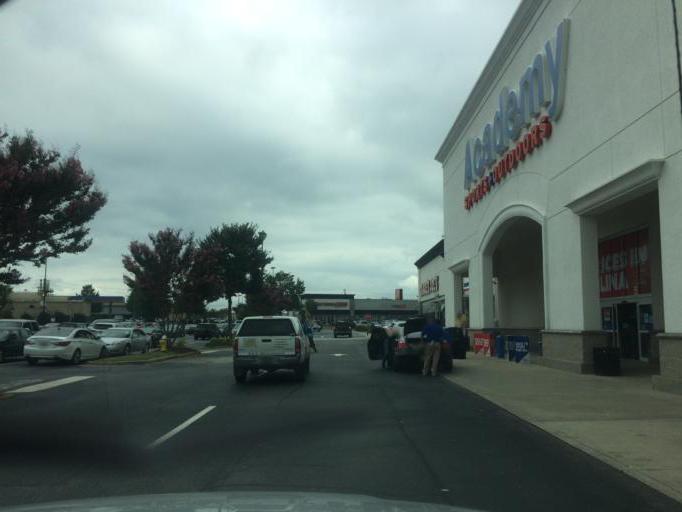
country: US
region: South Carolina
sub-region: Greenville County
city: Mauldin
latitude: 34.8291
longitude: -82.3064
